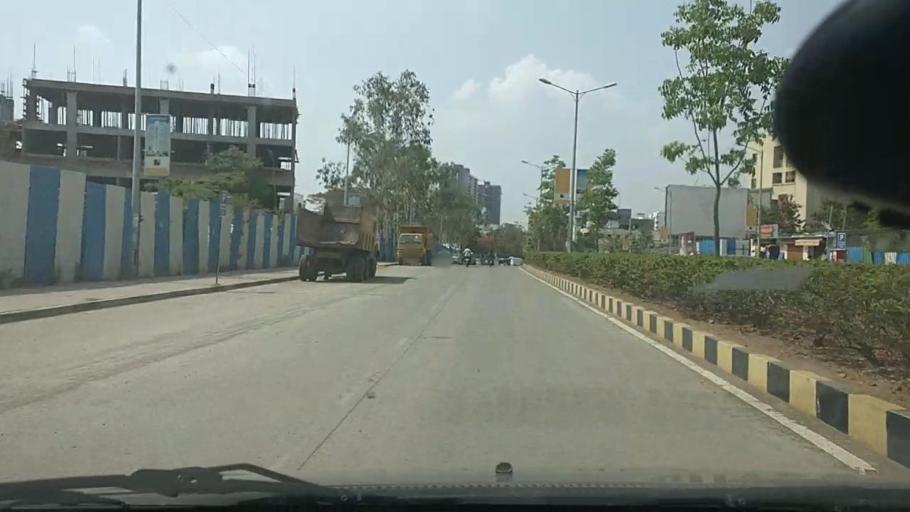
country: IN
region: Maharashtra
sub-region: Pune Division
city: Pimpri
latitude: 18.5720
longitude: 73.7747
